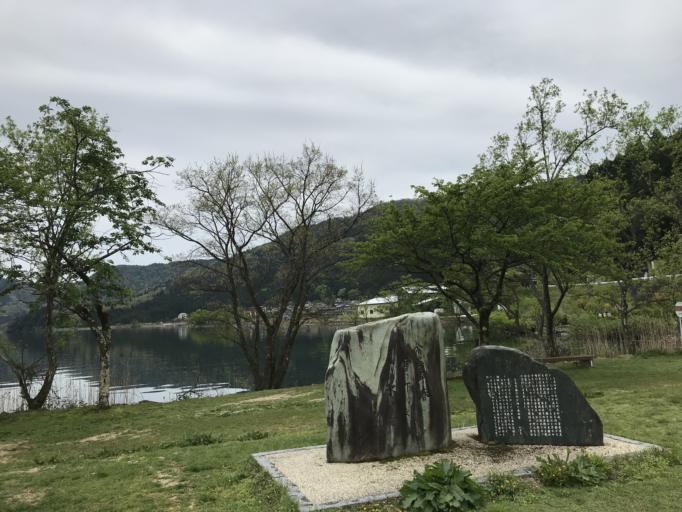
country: JP
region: Shiga Prefecture
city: Nagahama
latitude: 35.5324
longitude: 136.1908
